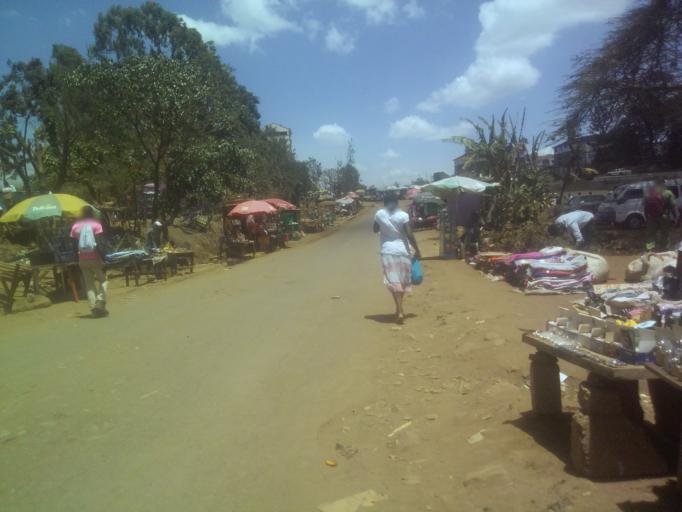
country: KE
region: Nairobi Area
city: Nairobi
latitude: -1.3057
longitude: 36.7878
